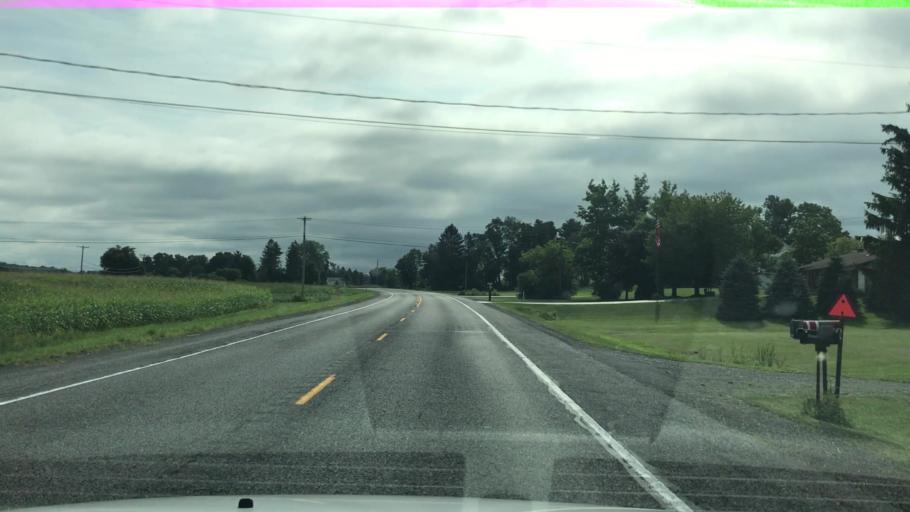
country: US
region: New York
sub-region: Erie County
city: Alden
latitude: 42.8354
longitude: -78.4077
